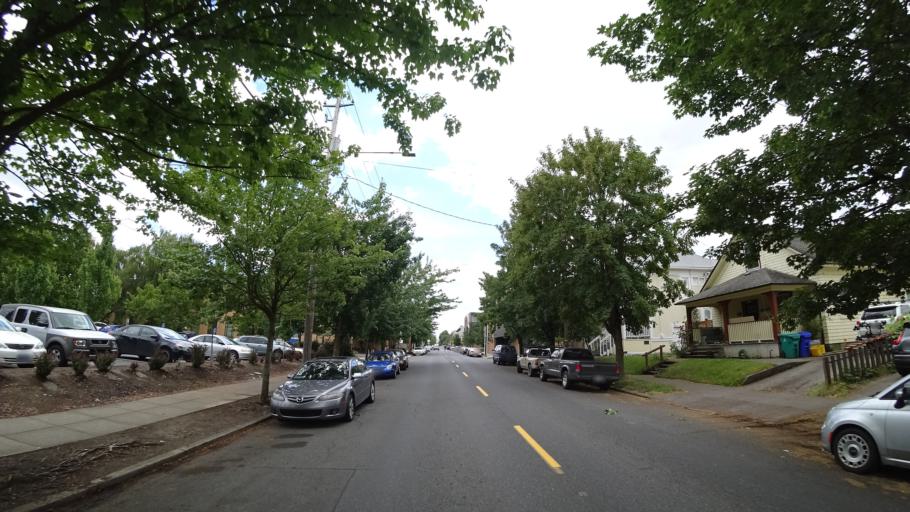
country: US
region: Oregon
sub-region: Multnomah County
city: Portland
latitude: 45.5645
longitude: -122.6750
